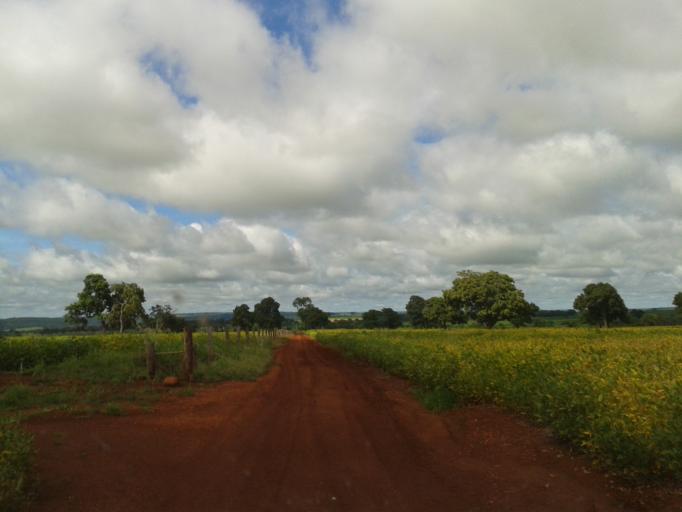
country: BR
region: Minas Gerais
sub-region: Santa Vitoria
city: Santa Vitoria
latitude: -18.7619
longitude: -49.8497
